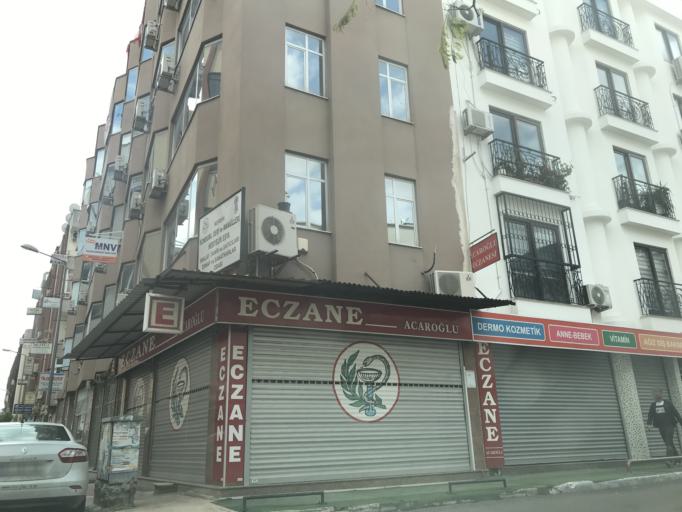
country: TR
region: Mersin
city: Mercin
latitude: 36.8019
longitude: 34.6296
